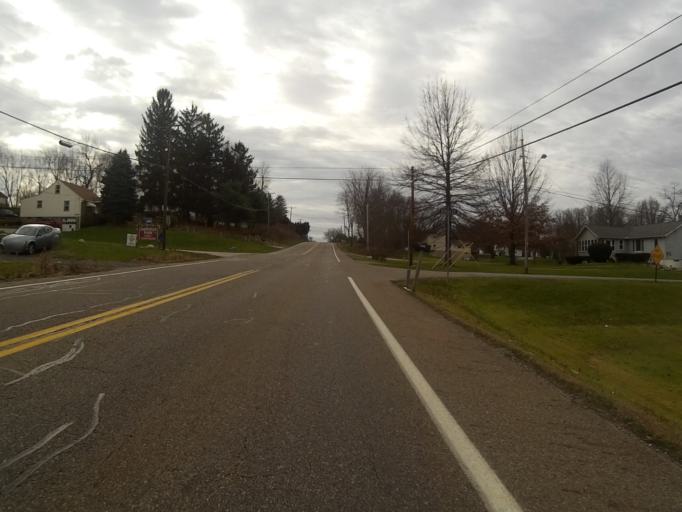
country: US
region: Ohio
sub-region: Portage County
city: Brimfield
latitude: 41.0730
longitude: -81.3471
